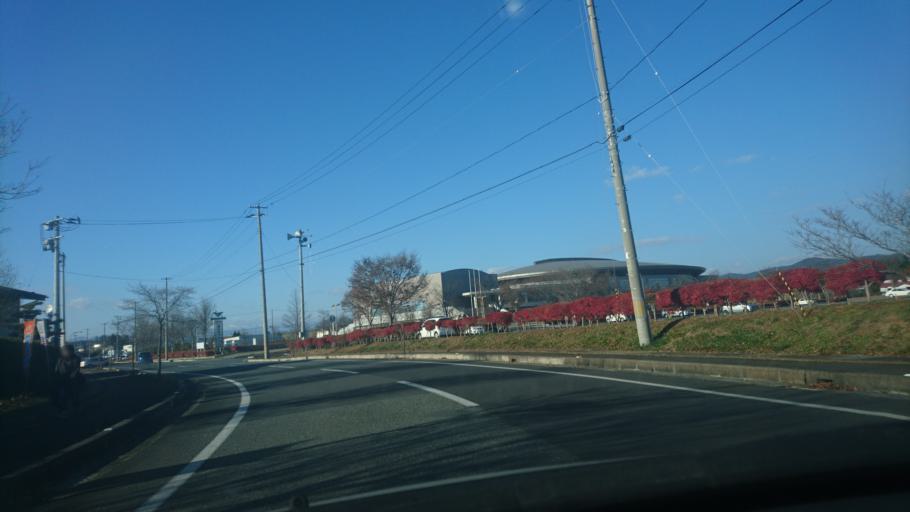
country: JP
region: Iwate
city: Ichinoseki
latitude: 38.9391
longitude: 141.1566
